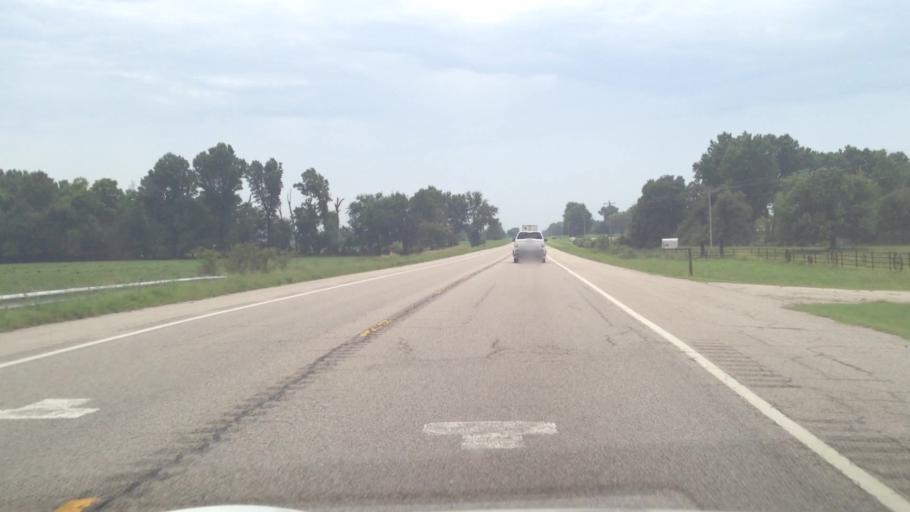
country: US
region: Missouri
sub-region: Jasper County
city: Carl Junction
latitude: 37.2019
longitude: -94.7048
